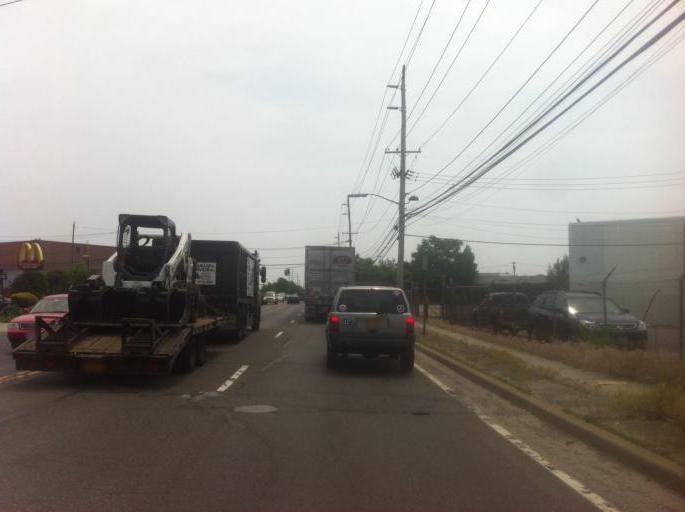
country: US
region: New York
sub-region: Nassau County
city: Bethpage
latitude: 40.7493
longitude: -73.5034
